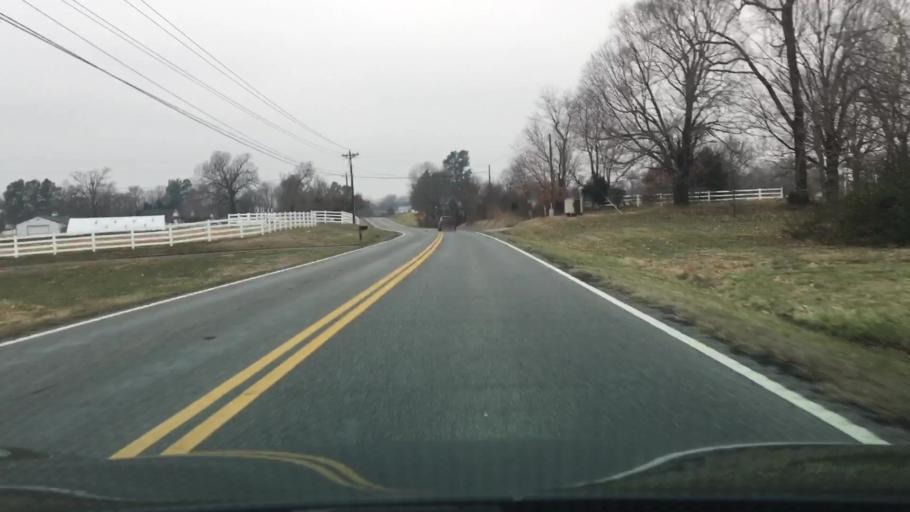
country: US
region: Kentucky
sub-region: Livingston County
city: Ledbetter
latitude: 36.9672
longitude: -88.4329
